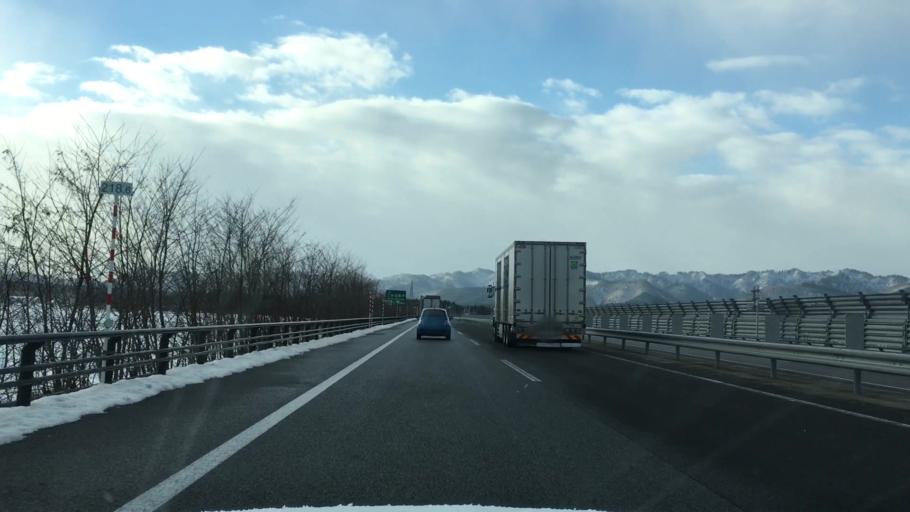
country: JP
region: Akita
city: Odate
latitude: 40.2574
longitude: 140.5213
